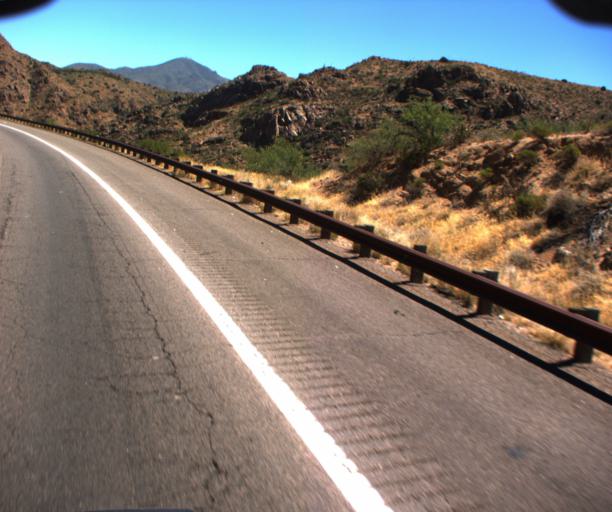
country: US
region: Arizona
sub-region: Gila County
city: Tonto Basin
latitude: 33.8388
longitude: -111.4686
